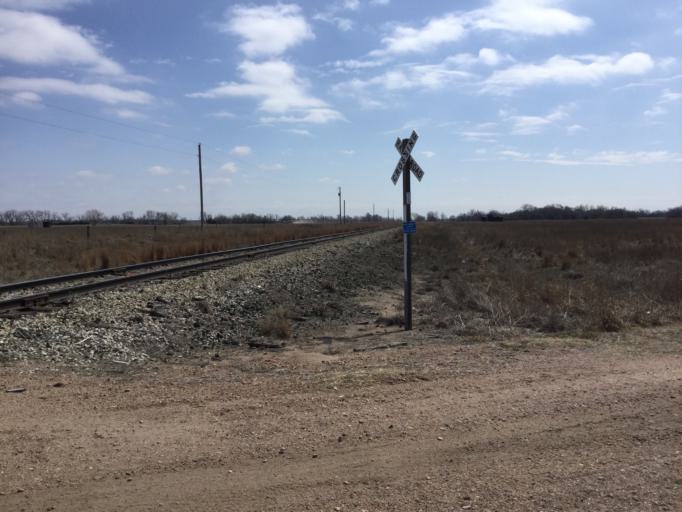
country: US
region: Kansas
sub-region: Barton County
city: Ellinwood
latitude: 38.3205
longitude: -98.4981
